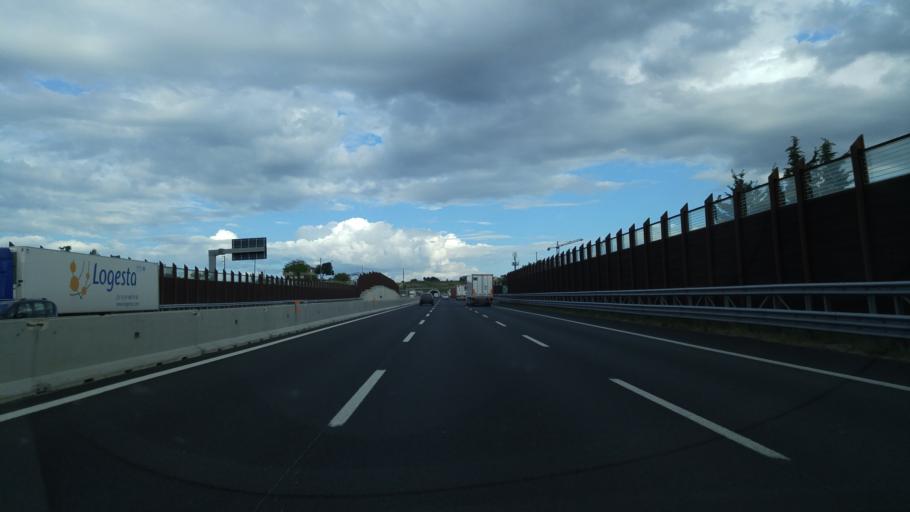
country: IT
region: Emilia-Romagna
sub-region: Provincia di Rimini
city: Riccione
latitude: 43.9837
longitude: 12.6448
